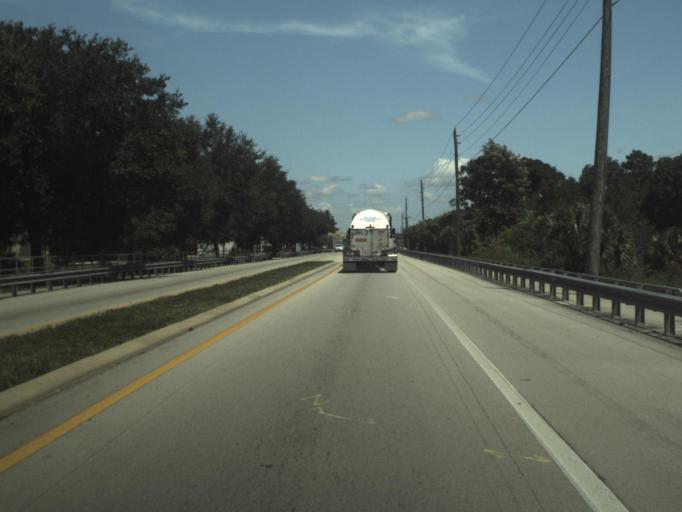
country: US
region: Florida
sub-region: Martin County
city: Indiantown
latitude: 27.0261
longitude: -80.4752
